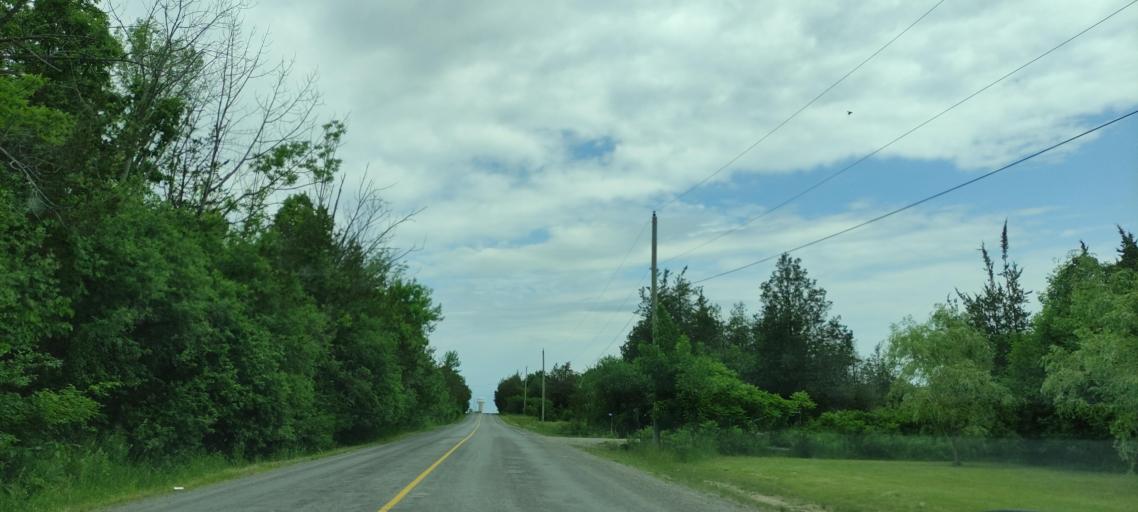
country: CA
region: Ontario
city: Quinte West
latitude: 44.0826
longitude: -77.5972
